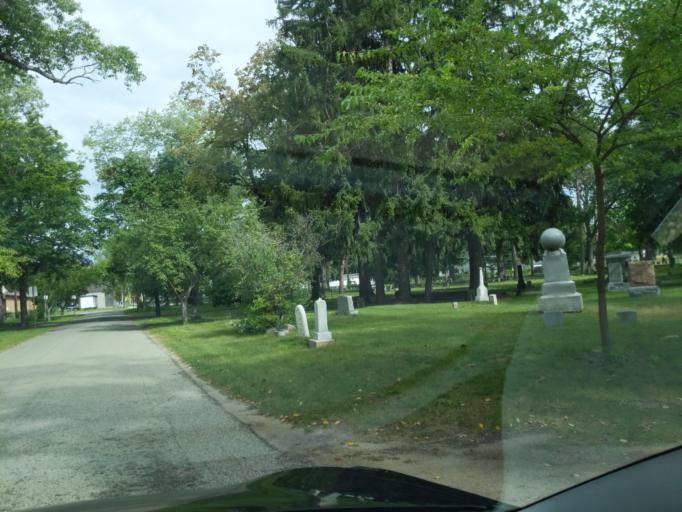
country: US
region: Michigan
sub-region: Grand Traverse County
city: Traverse City
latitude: 44.7576
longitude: -85.5890
